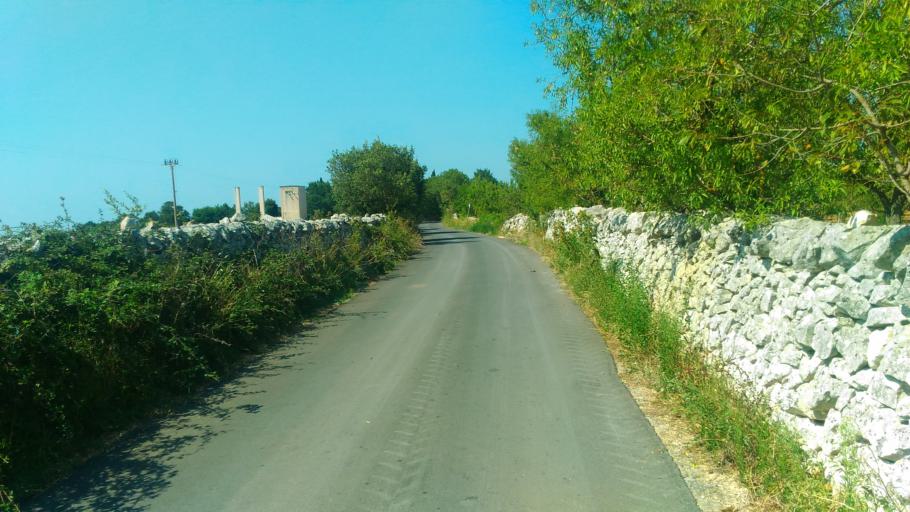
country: IT
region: Apulia
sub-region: Provincia di Bari
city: Alberobello
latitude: 40.8016
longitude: 17.1838
